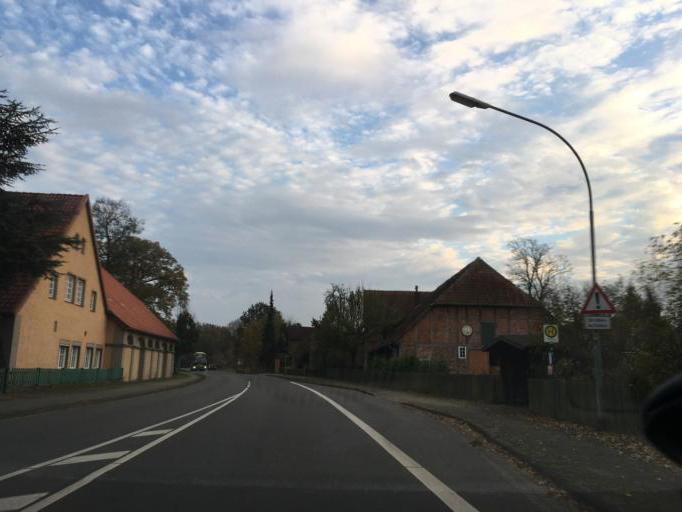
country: DE
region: Lower Saxony
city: Hambuhren
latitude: 52.6961
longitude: 9.9825
